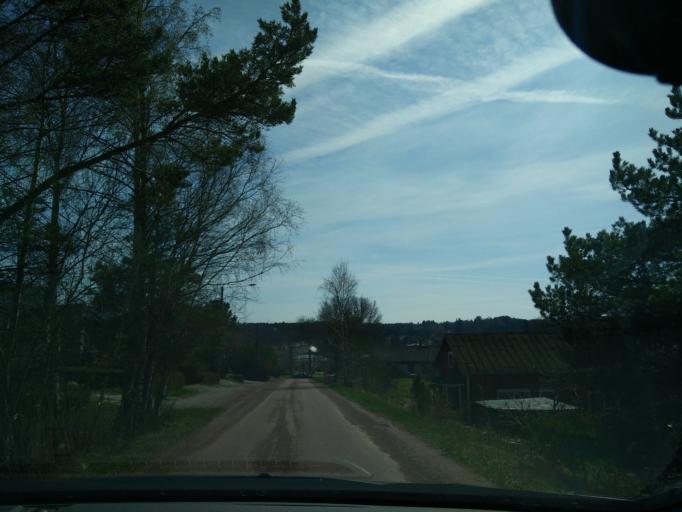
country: AX
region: Alands landsbygd
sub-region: Finstroem
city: Finstroem
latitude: 60.2340
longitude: 19.9887
